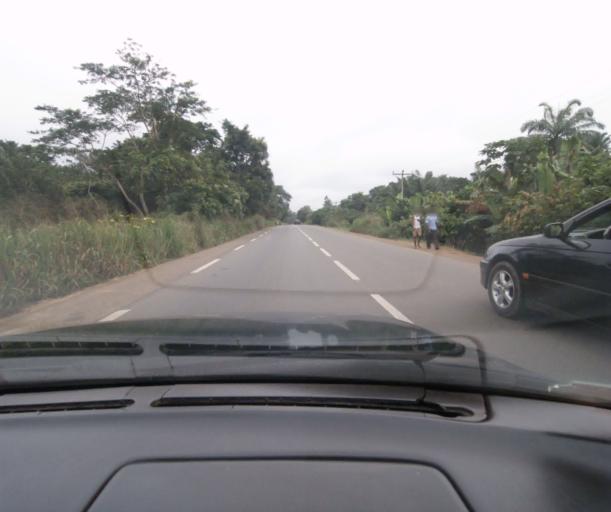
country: CM
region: Centre
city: Obala
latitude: 4.1815
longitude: 11.4679
